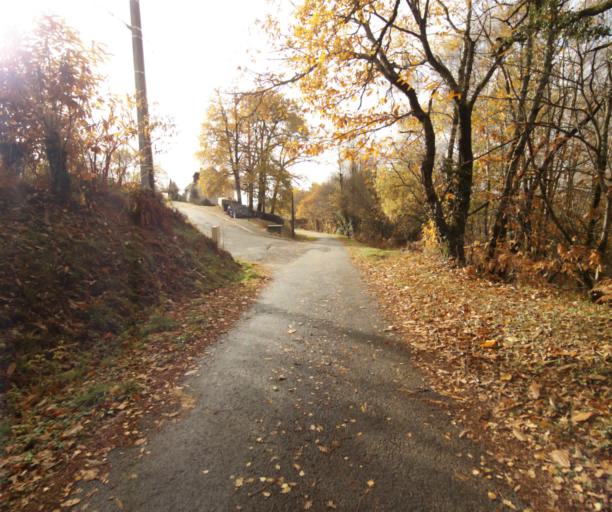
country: FR
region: Limousin
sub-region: Departement de la Correze
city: Cornil
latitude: 45.2163
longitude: 1.6387
